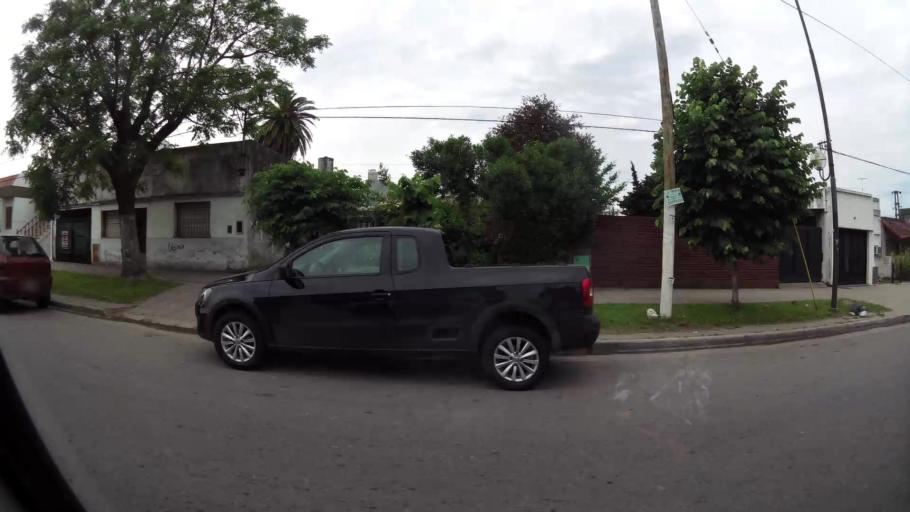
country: AR
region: Buenos Aires
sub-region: Partido de La Plata
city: La Plata
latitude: -34.9285
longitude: -57.9996
